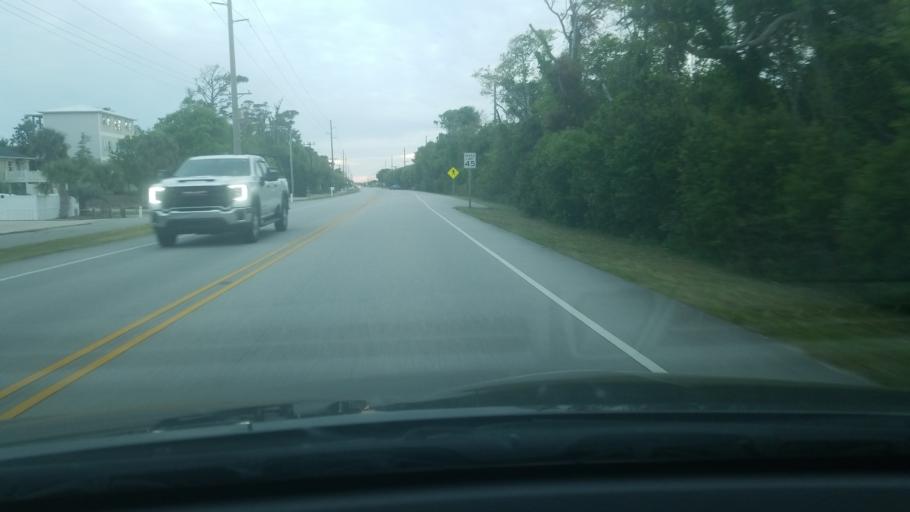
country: US
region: North Carolina
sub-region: Carteret County
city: Cape Carteret
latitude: 34.6675
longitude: -77.0218
